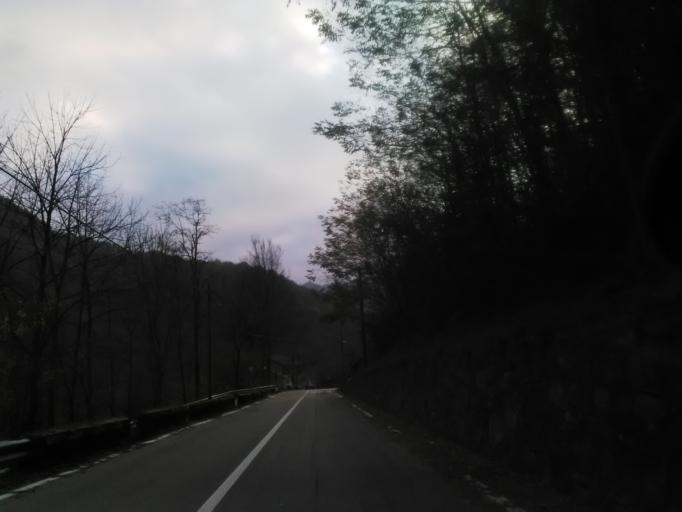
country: IT
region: Piedmont
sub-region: Provincia di Vercelli
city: Varallo
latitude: 45.8306
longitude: 8.2549
